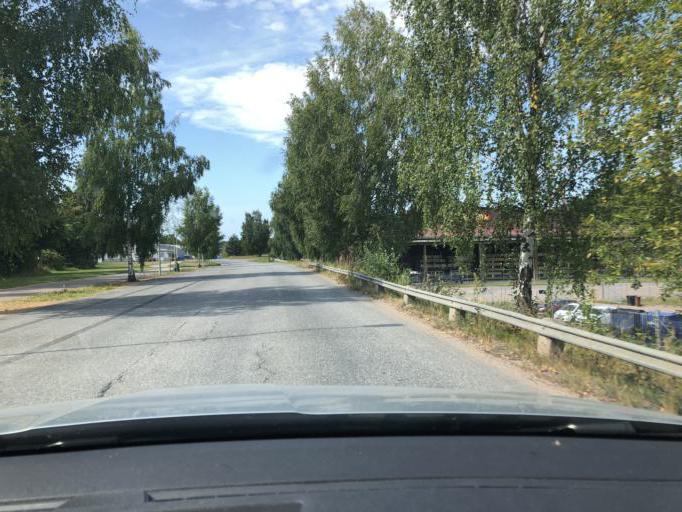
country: SE
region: Dalarna
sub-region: Avesta Kommun
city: Avesta
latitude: 60.1464
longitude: 16.1869
